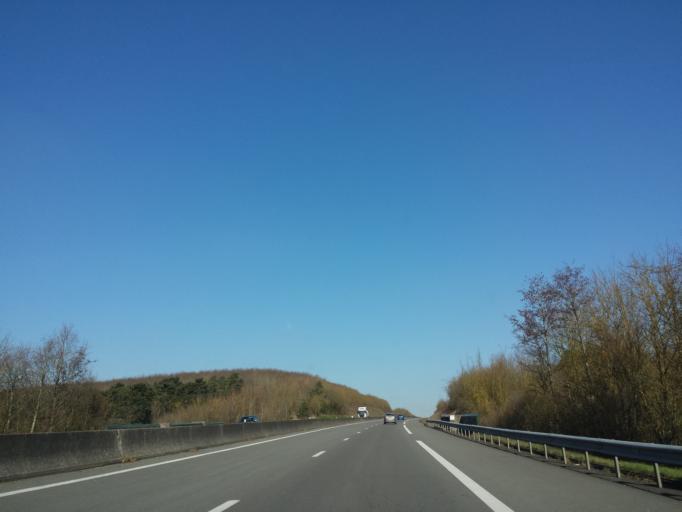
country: FR
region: Picardie
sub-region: Departement de la Somme
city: Conty
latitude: 49.7482
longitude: 2.2303
